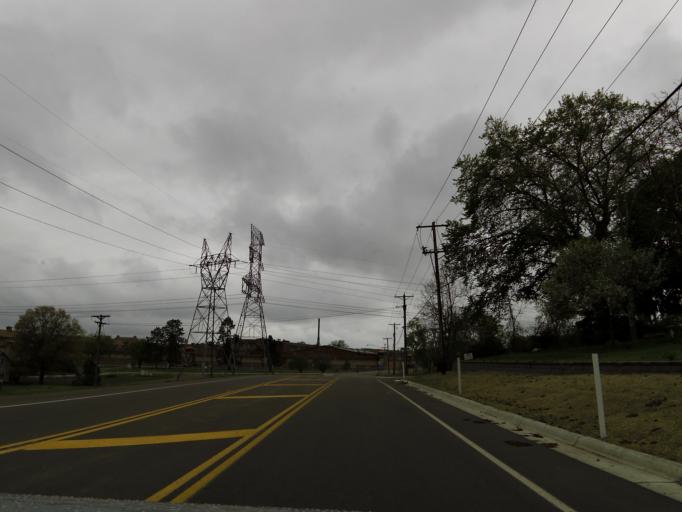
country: US
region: Minnesota
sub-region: Washington County
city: Oak Park Heights
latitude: 45.0314
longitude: -92.7915
